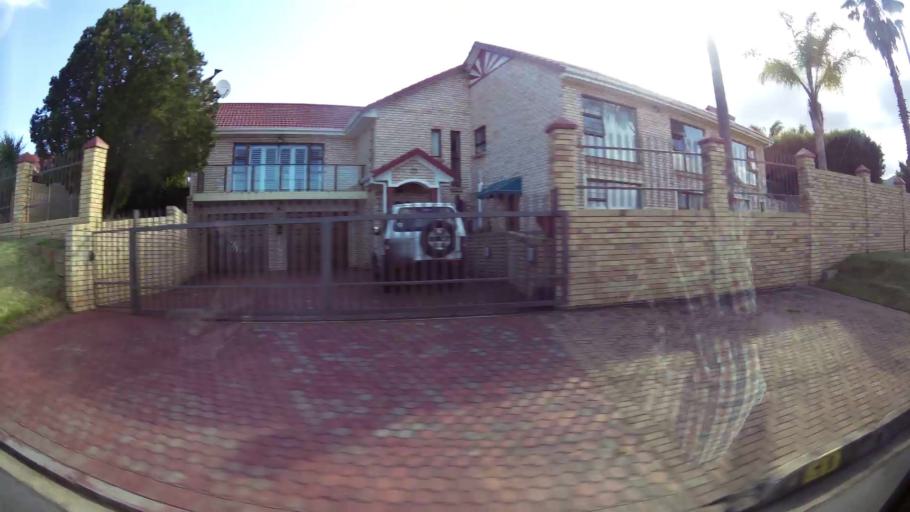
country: ZA
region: Western Cape
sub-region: Eden District Municipality
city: George
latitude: -33.9587
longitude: 22.4899
